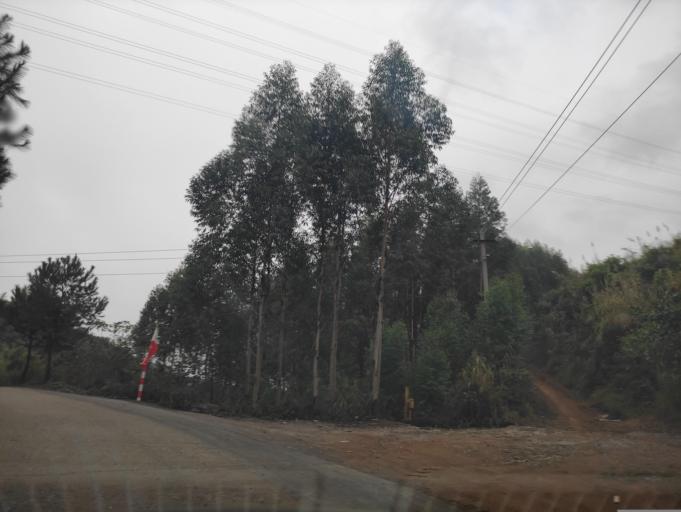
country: CN
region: Guangxi Zhuangzu Zizhiqu
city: Baise City
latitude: 23.8545
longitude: 106.7548
